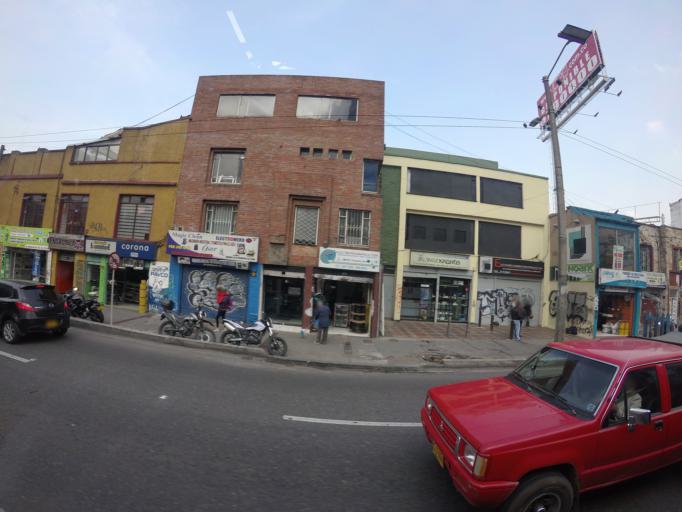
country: CO
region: Bogota D.C.
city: Barrio San Luis
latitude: 4.6535
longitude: -74.0639
